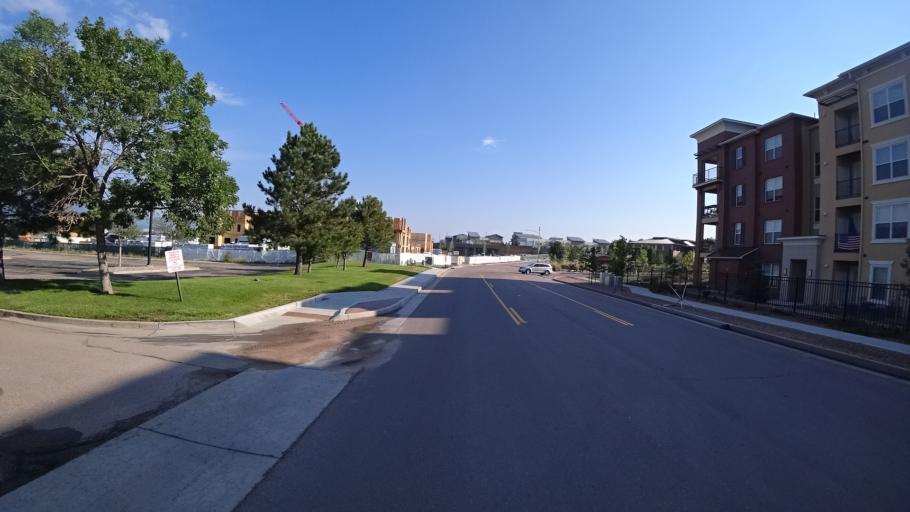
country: US
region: Colorado
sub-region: El Paso County
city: Air Force Academy
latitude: 38.9602
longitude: -104.7962
